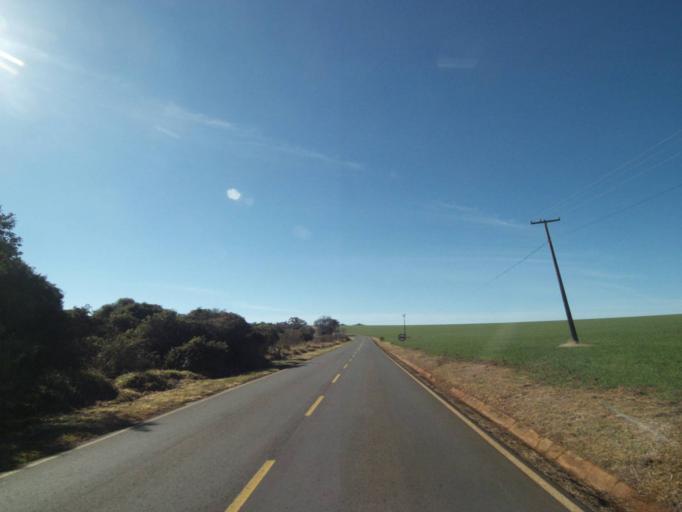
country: BR
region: Parana
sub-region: Tibagi
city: Tibagi
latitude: -24.5201
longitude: -50.3427
